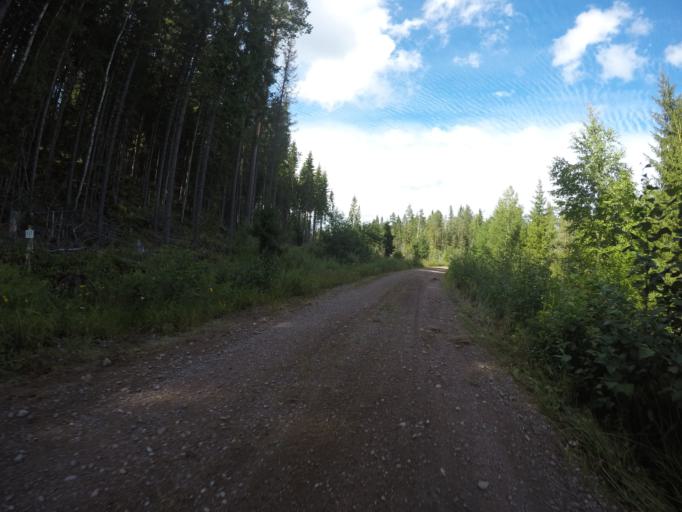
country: SE
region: Dalarna
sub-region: Ludvika Kommun
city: Abborrberget
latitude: 60.0283
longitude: 14.6016
